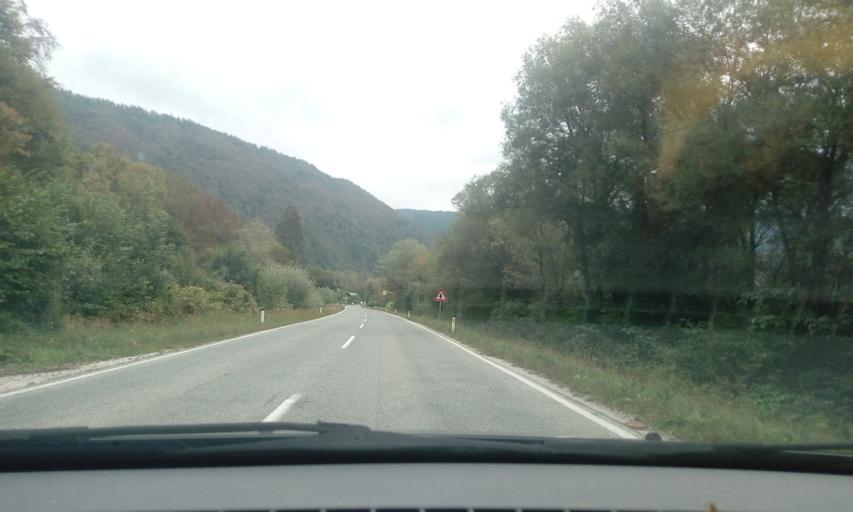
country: SI
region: Bohinj
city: Bohinjska Bistrica
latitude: 46.2888
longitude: 13.9948
